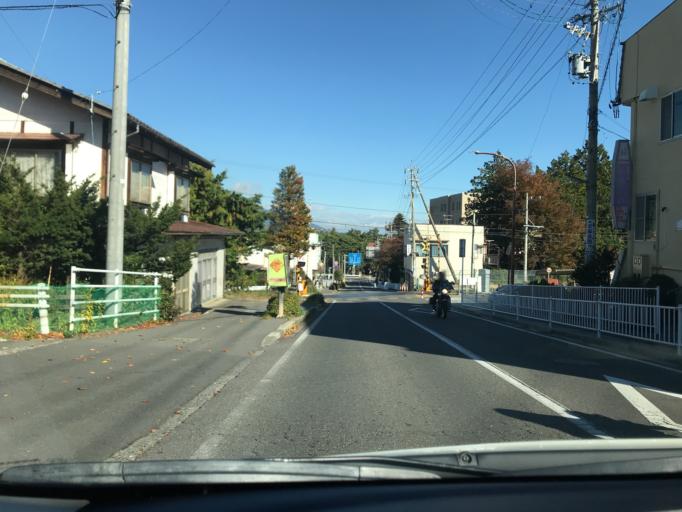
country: JP
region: Nagano
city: Toyoshina
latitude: 36.1995
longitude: 137.8557
